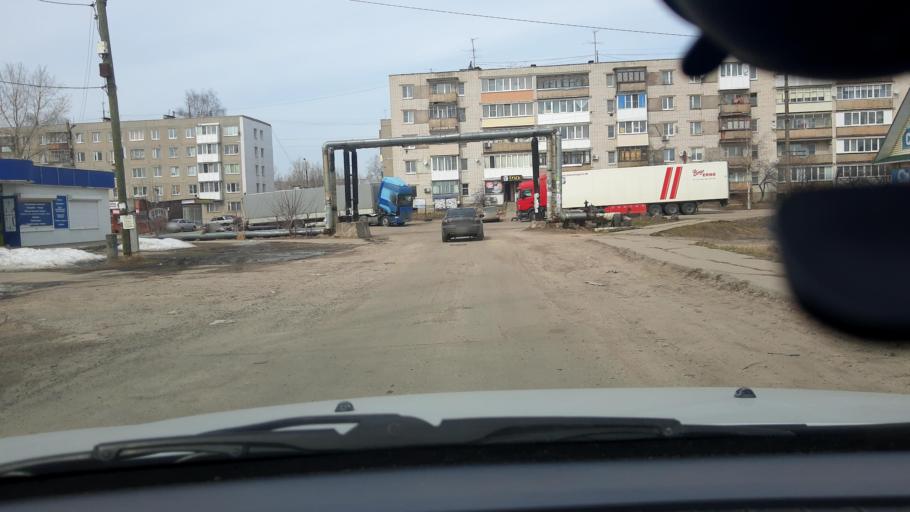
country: RU
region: Nizjnij Novgorod
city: Gidrotorf
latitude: 56.4637
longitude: 43.5380
